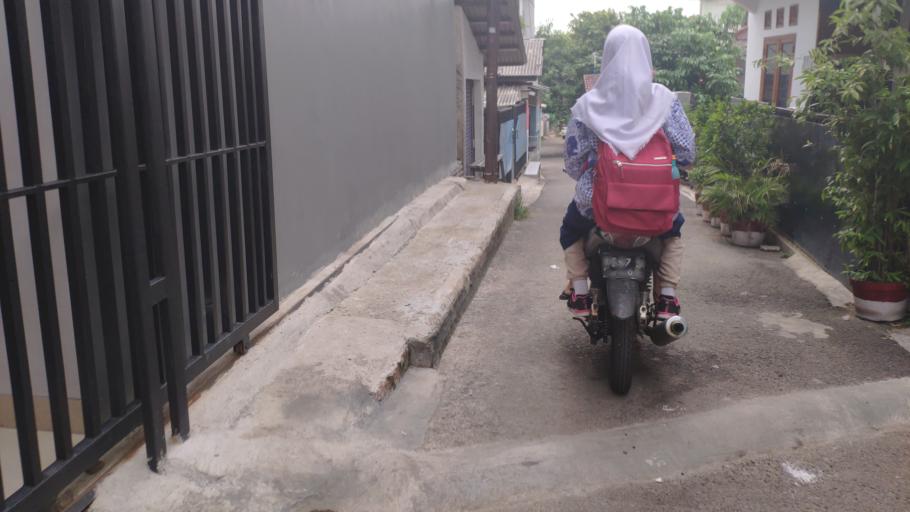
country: ID
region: Jakarta Raya
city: Jakarta
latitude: -6.2701
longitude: 106.8297
